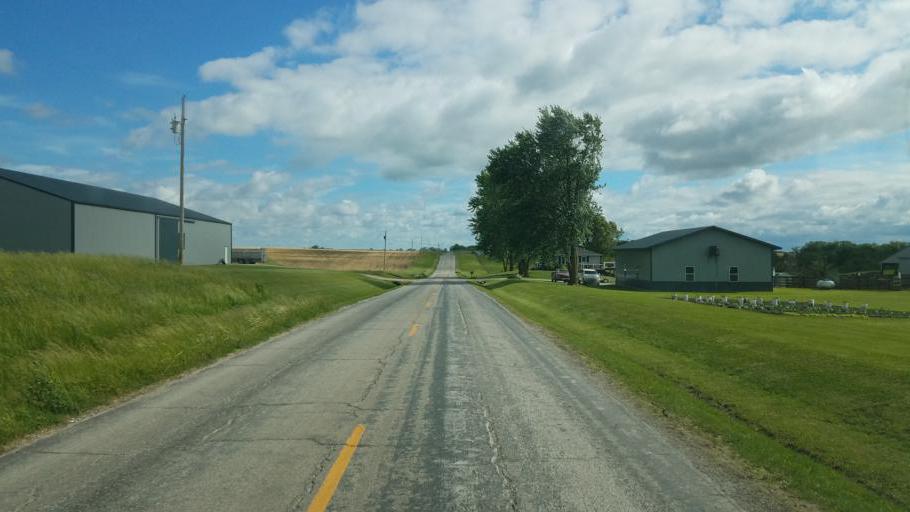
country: US
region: Missouri
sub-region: Mercer County
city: Princeton
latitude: 40.2711
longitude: -93.6757
